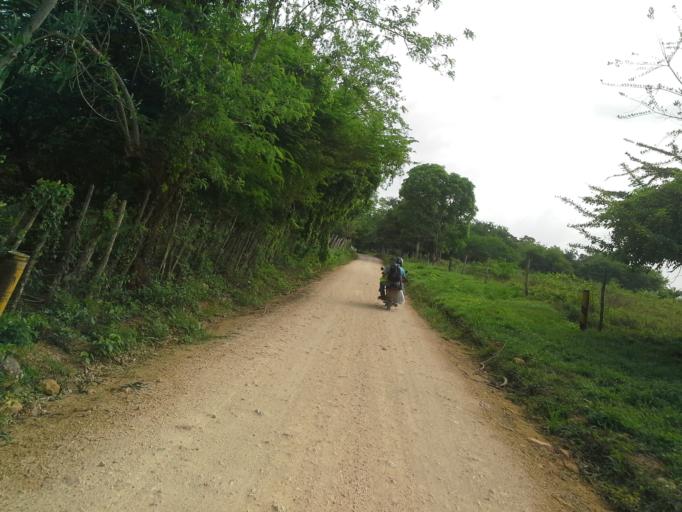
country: CO
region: Cordoba
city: Chima
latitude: 9.1621
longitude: -75.6150
